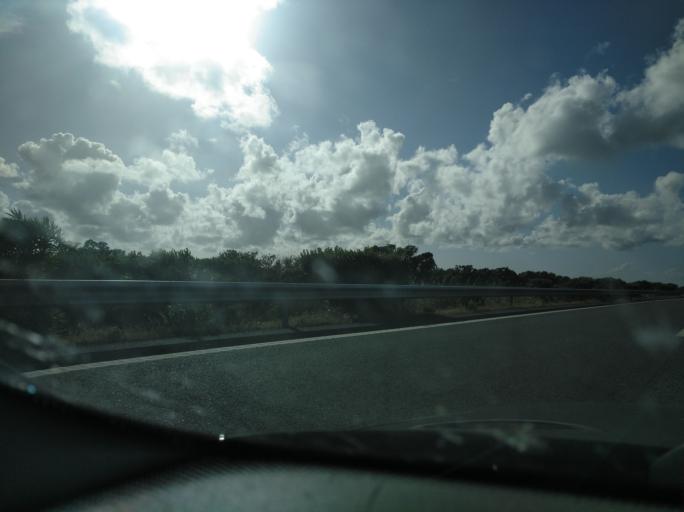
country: PT
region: Setubal
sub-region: Grandola
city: Grandola
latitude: 38.1745
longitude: -8.4986
